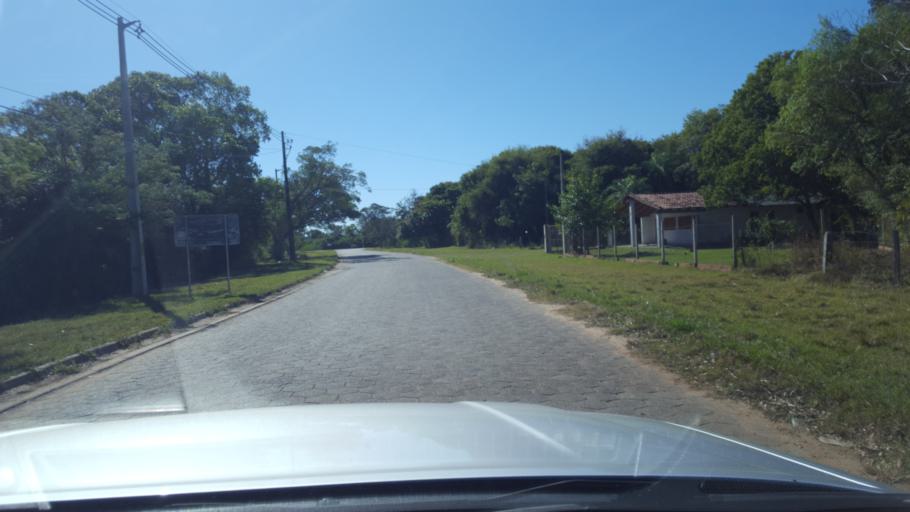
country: PY
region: Neembucu
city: Pilar
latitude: -26.8715
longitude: -58.3179
